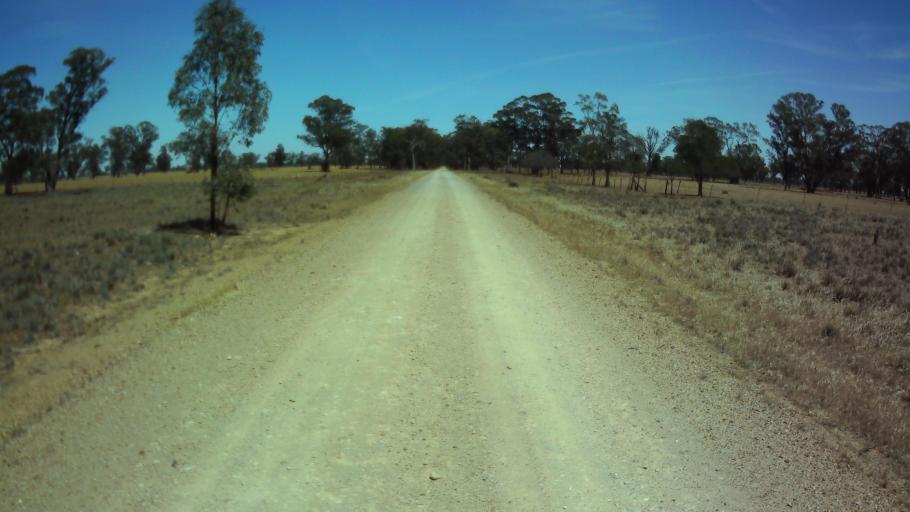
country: AU
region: New South Wales
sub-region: Weddin
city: Grenfell
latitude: -34.0700
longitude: 147.9031
